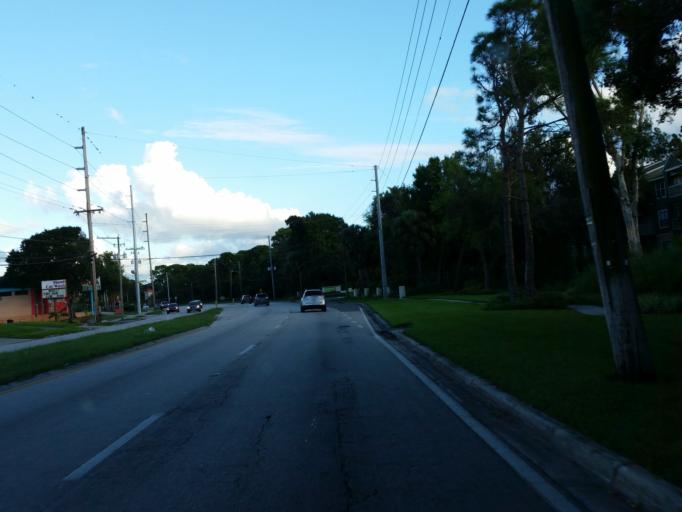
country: US
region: Florida
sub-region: Hillsborough County
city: Town 'n' Country
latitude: 27.9836
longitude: -82.5687
